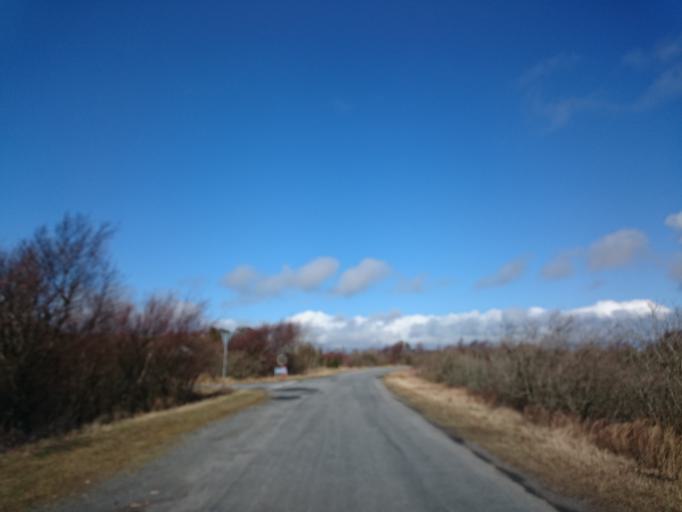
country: DK
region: North Denmark
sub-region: Frederikshavn Kommune
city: Strandby
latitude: 57.6534
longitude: 10.4095
